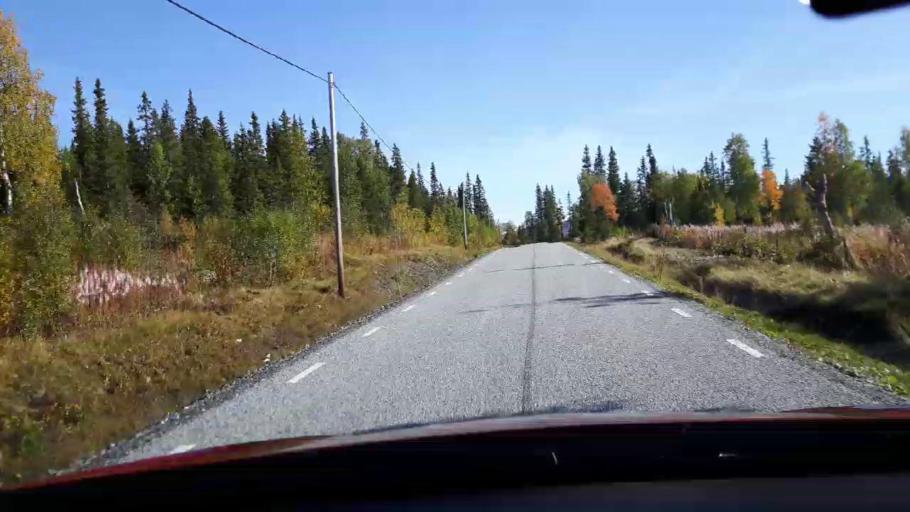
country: NO
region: Nord-Trondelag
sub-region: Royrvik
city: Royrvik
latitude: 64.8138
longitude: 14.1541
